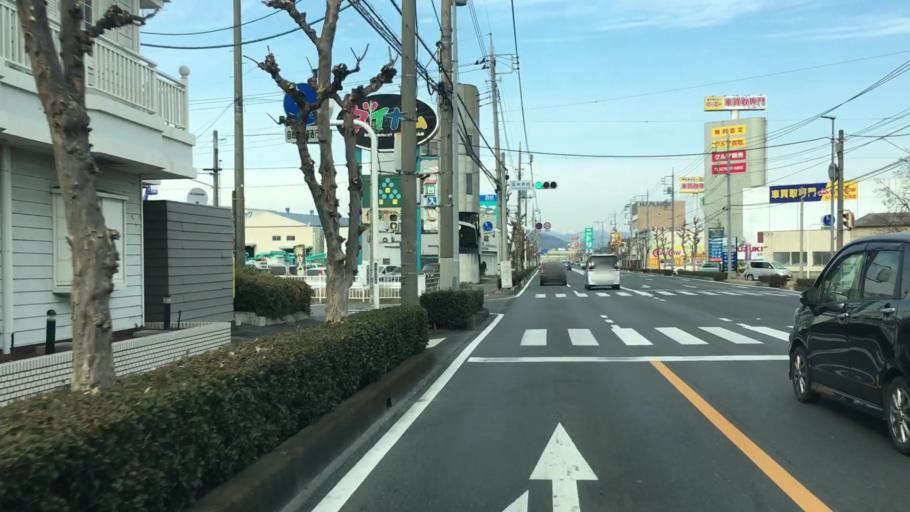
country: JP
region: Gunma
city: Ota
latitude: 36.2631
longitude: 139.3769
